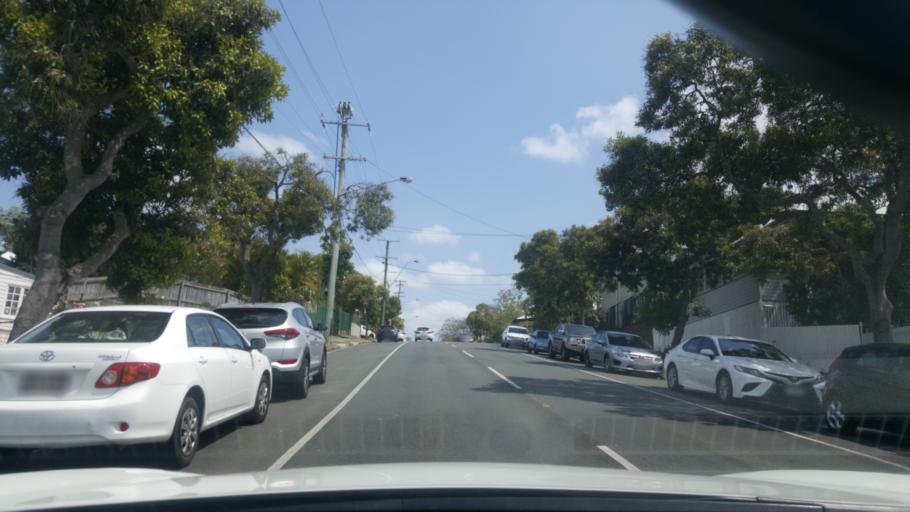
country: AU
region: Queensland
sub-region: Brisbane
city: South Brisbane
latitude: -27.4886
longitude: 153.0260
